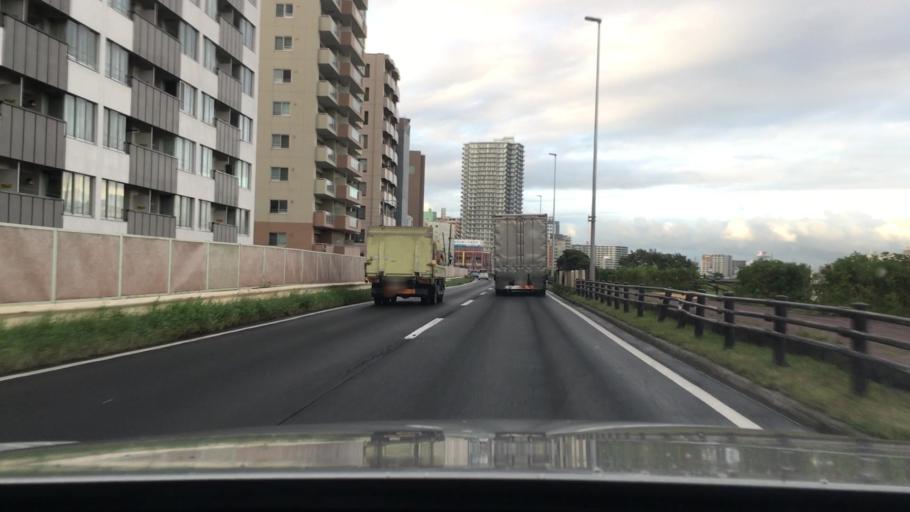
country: JP
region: Hokkaido
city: Sapporo
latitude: 43.0441
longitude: 141.3581
